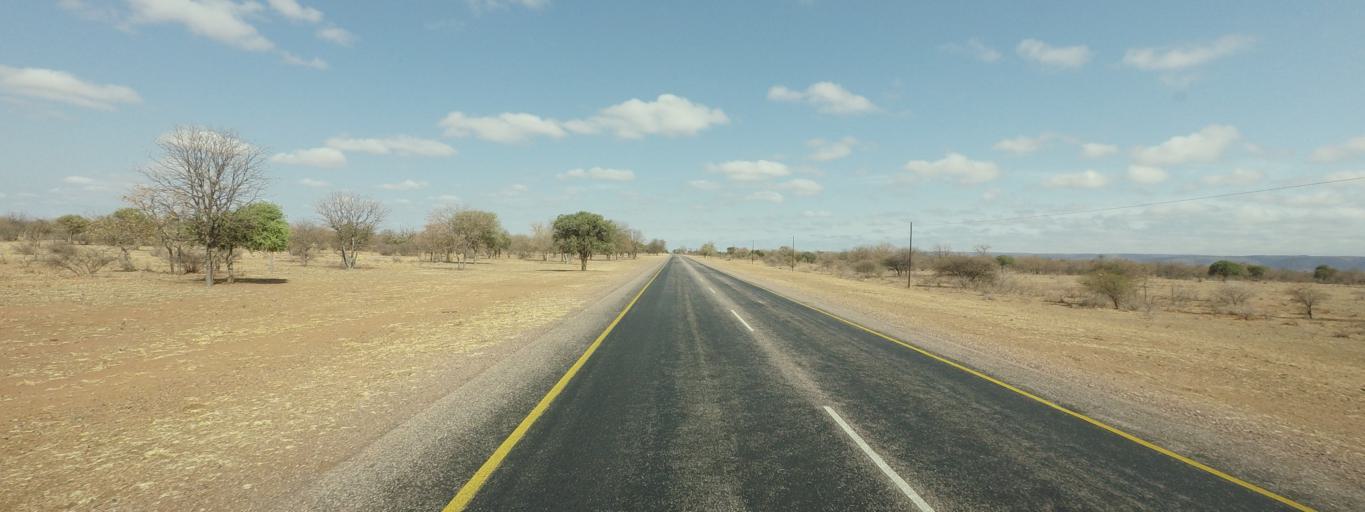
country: BW
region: Central
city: Ramokgonami
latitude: -22.7955
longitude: 27.4688
